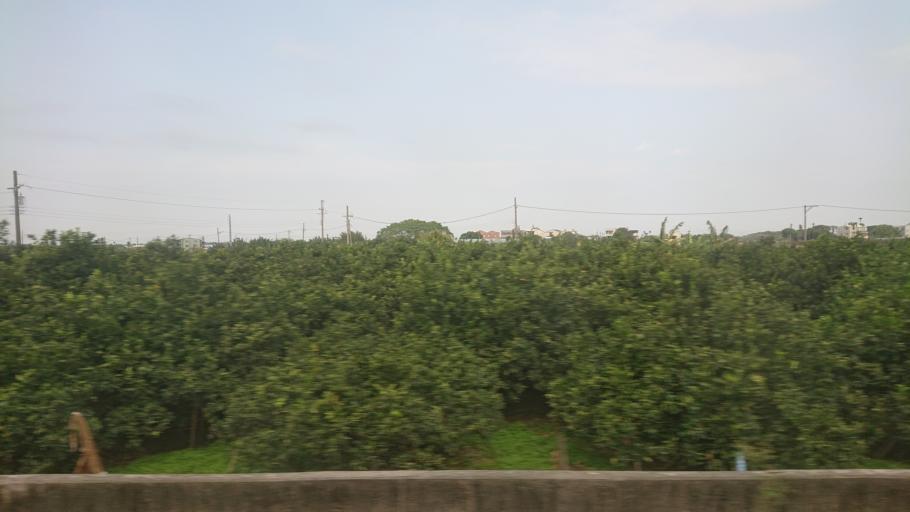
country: TW
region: Taiwan
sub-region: Yunlin
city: Douliu
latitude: 23.7371
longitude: 120.5853
